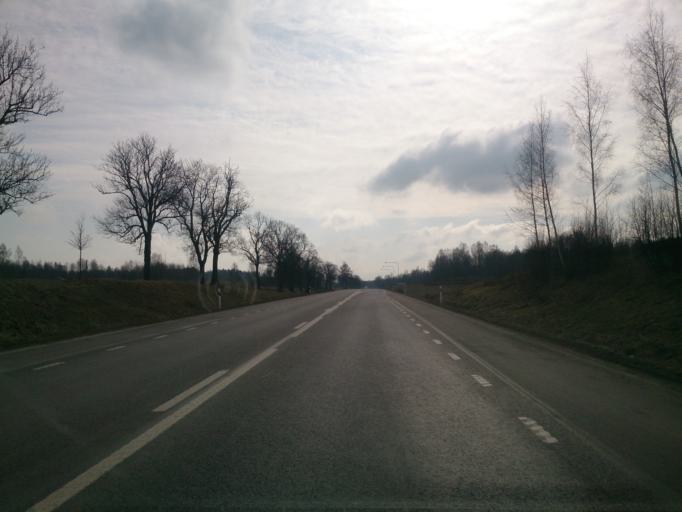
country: SE
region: OEstergoetland
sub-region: Atvidabergs Kommun
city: Atvidaberg
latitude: 58.2278
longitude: 15.9664
